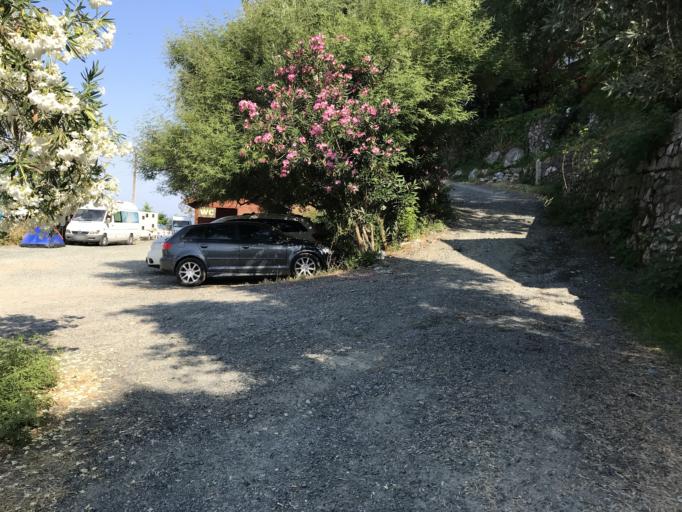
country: TR
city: Dalyan
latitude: 36.8737
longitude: 28.6028
